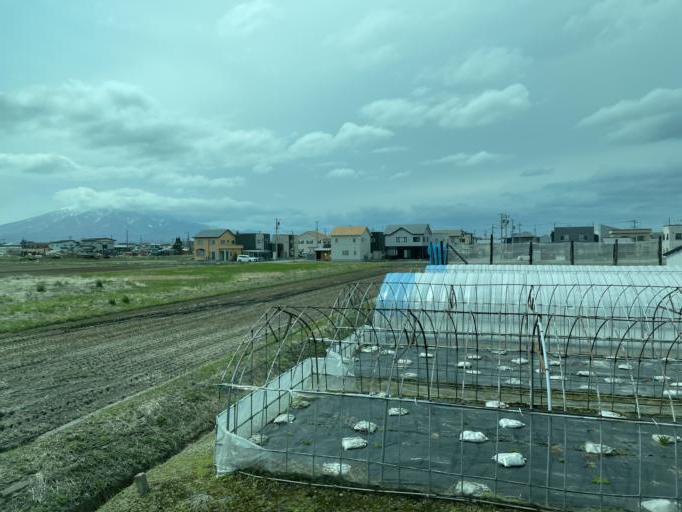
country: JP
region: Aomori
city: Goshogawara
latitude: 40.7695
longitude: 140.4344
